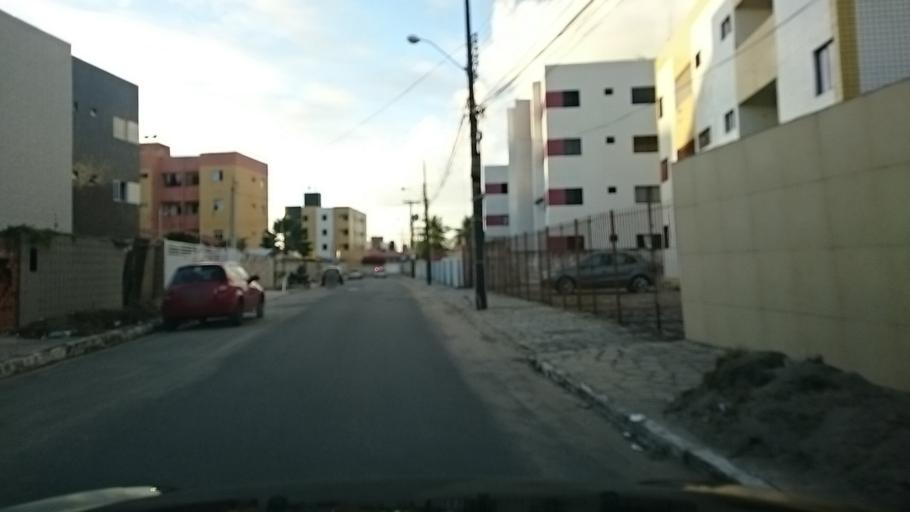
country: BR
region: Paraiba
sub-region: Joao Pessoa
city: Joao Pessoa
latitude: -7.1529
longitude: -34.8357
